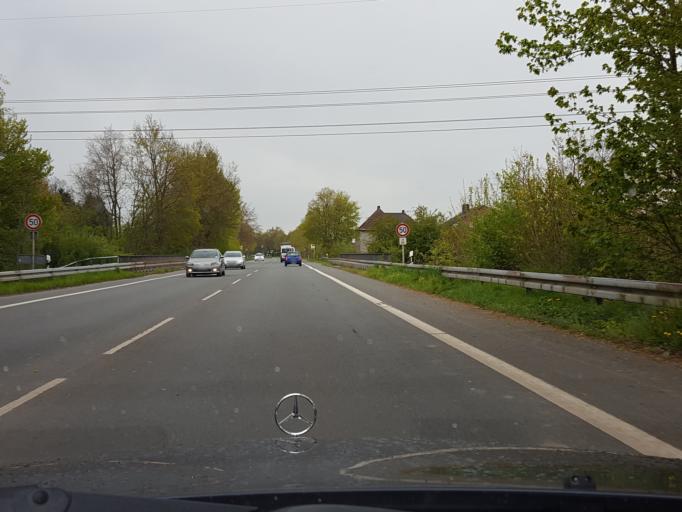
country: DE
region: North Rhine-Westphalia
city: Waltrop
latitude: 51.6337
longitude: 7.3791
